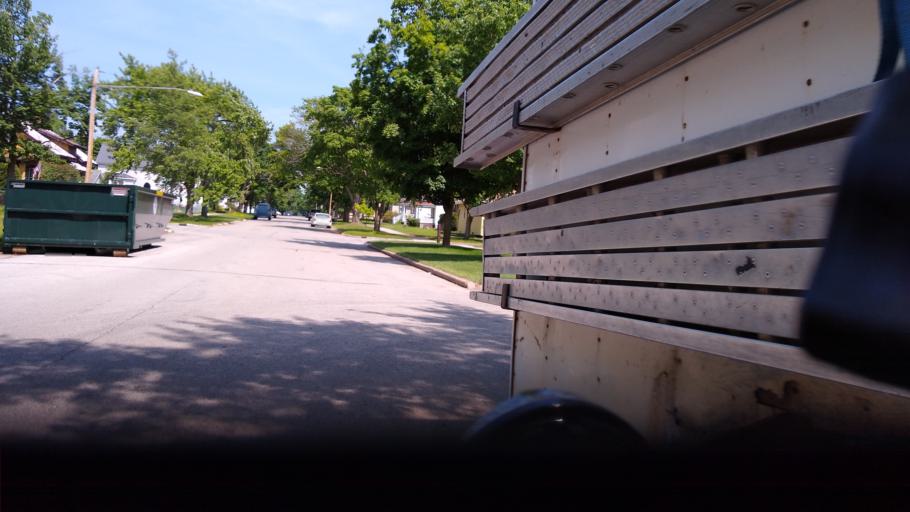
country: US
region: Michigan
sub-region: Delta County
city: Escanaba
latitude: 45.7373
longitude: -87.0663
